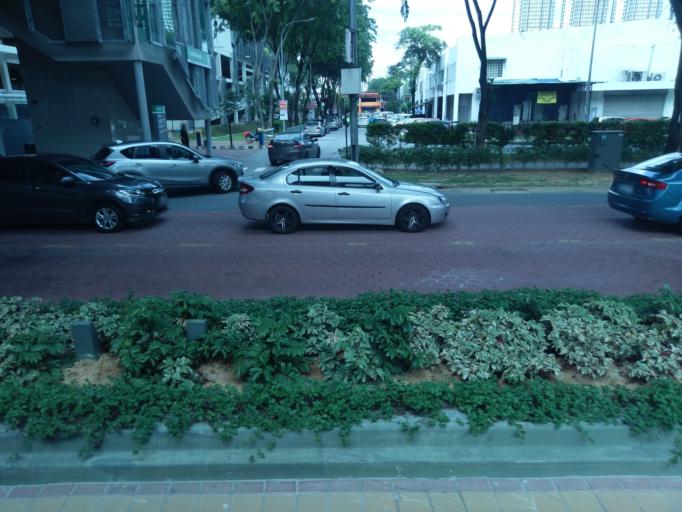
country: MY
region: Selangor
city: Subang Jaya
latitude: 3.0653
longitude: 101.6018
